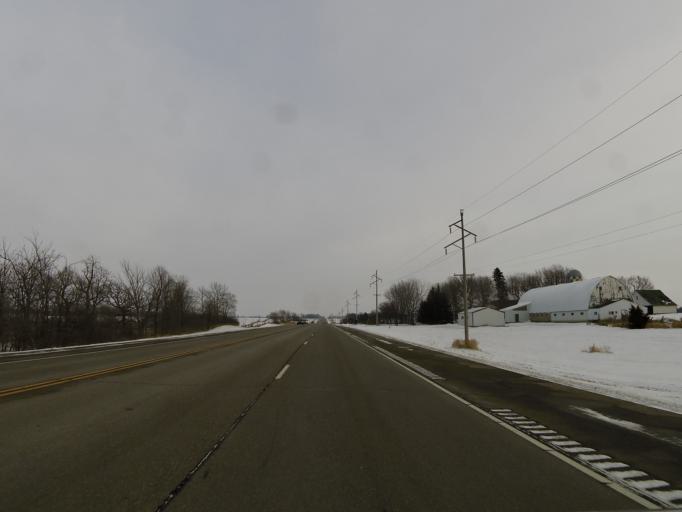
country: US
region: Minnesota
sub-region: Carver County
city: Mayer
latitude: 44.9055
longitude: -93.8535
